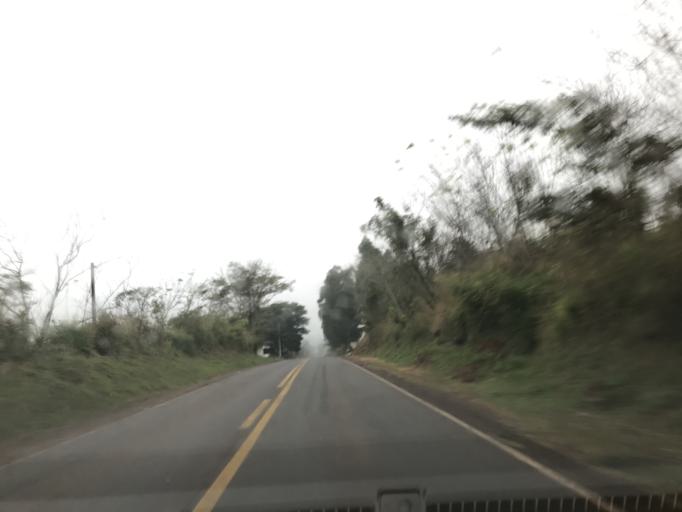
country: PY
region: Canindeyu
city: Salto del Guaira
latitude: -24.1031
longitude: -54.1043
